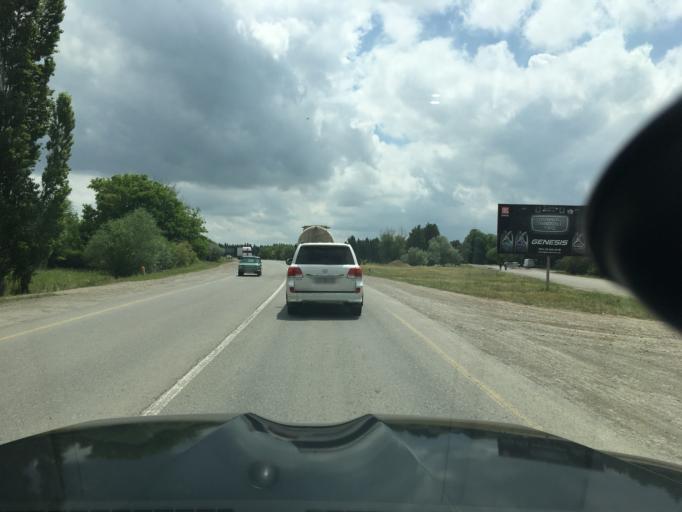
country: AZ
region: Tovuz
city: Qaraxanli
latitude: 41.0309
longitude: 45.5959
